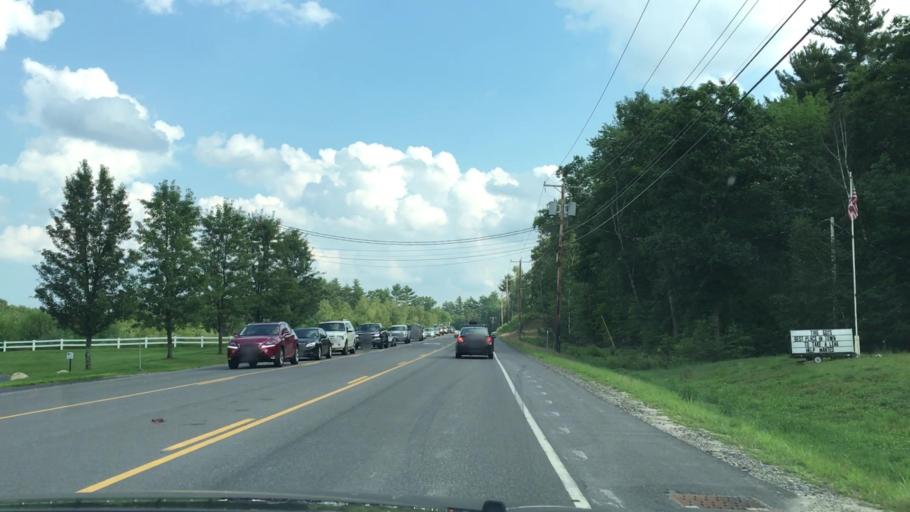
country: US
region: New Hampshire
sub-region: Strafford County
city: Farmington
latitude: 43.3656
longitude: -71.0380
